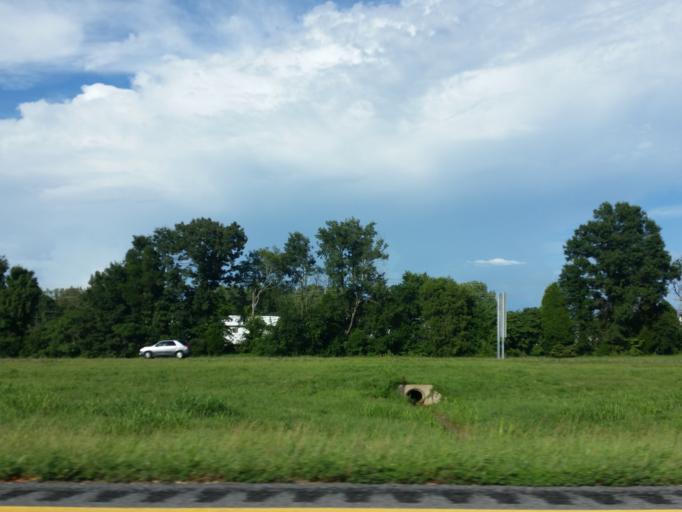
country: US
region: Tennessee
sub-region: Montgomery County
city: Clarksville
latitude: 36.5821
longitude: -87.2673
